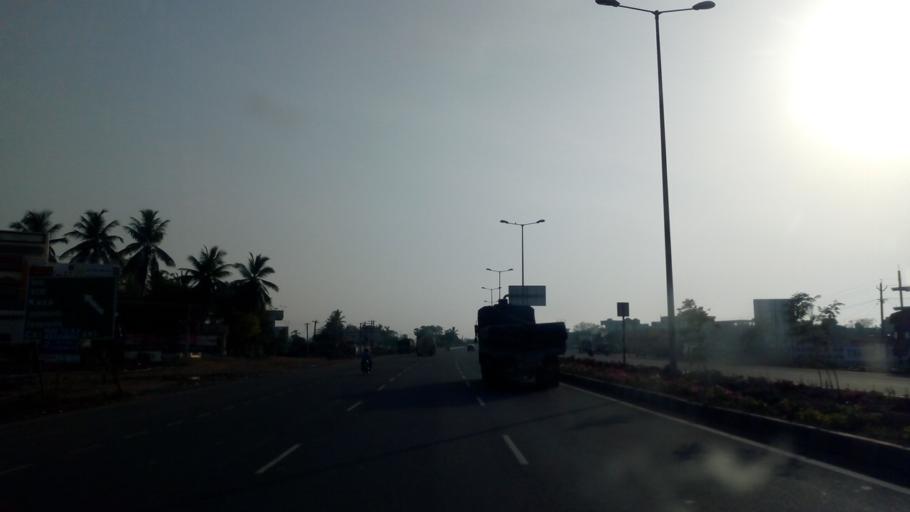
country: IN
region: Andhra Pradesh
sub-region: Guntur
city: Mangalagiri
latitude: 16.3878
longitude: 80.5356
